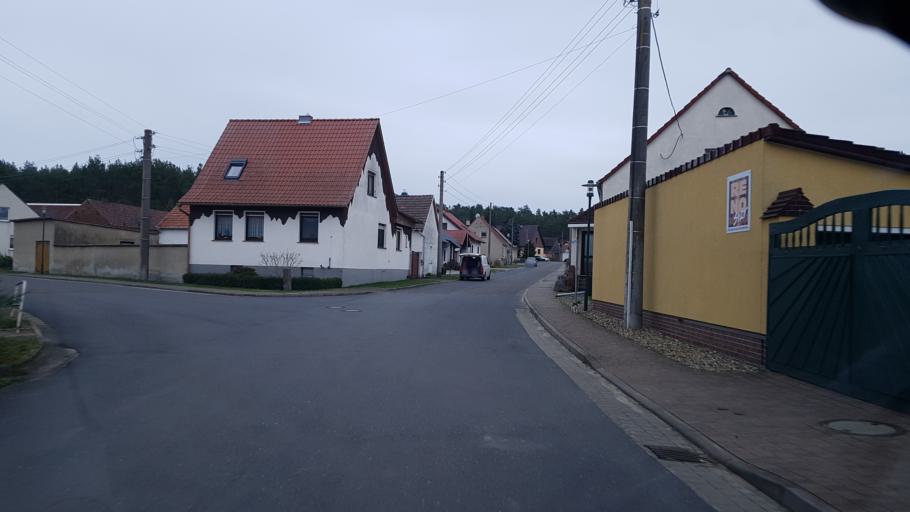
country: DE
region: Brandenburg
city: Schlieben
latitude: 51.7118
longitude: 13.3006
